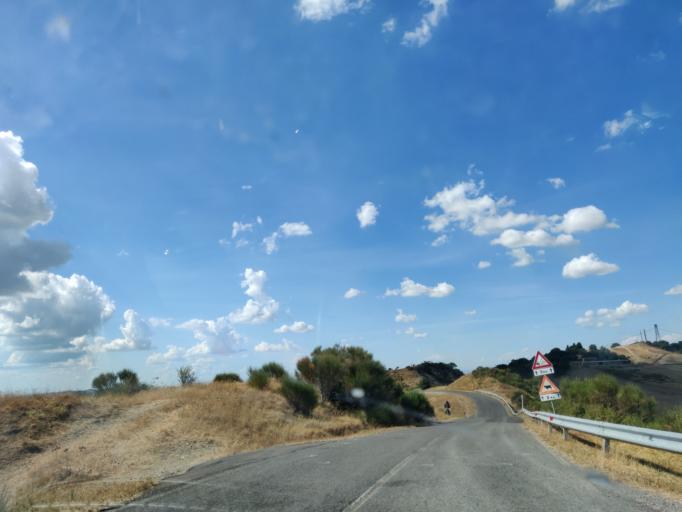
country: IT
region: Tuscany
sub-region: Provincia di Siena
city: Radicofani
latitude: 42.9518
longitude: 11.7299
